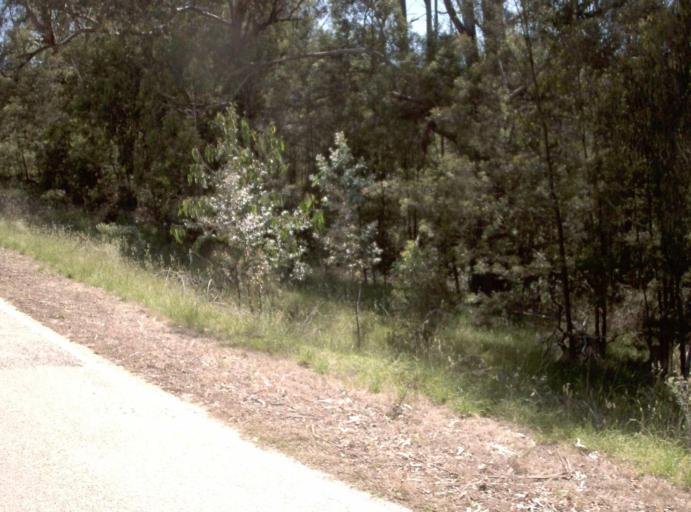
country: AU
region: Victoria
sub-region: East Gippsland
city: Lakes Entrance
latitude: -37.3406
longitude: 148.2284
